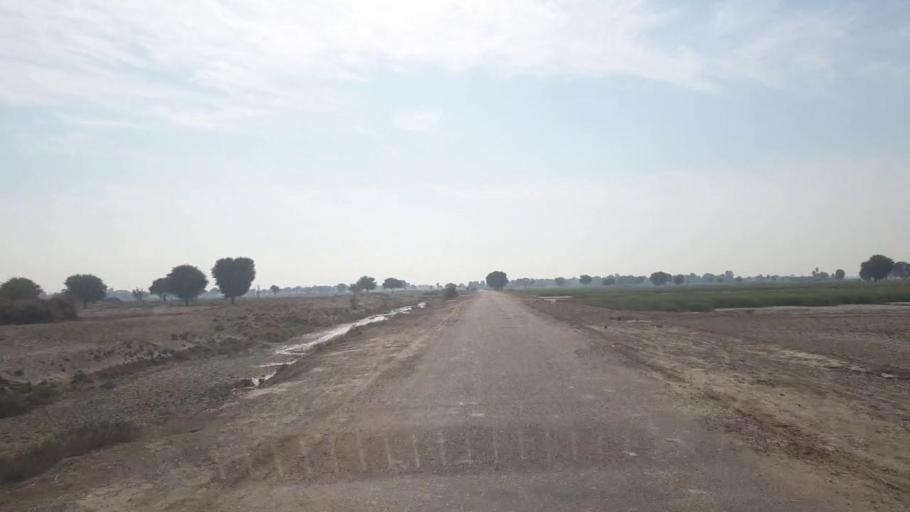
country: PK
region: Sindh
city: Shahpur Chakar
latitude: 26.1595
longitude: 68.5150
